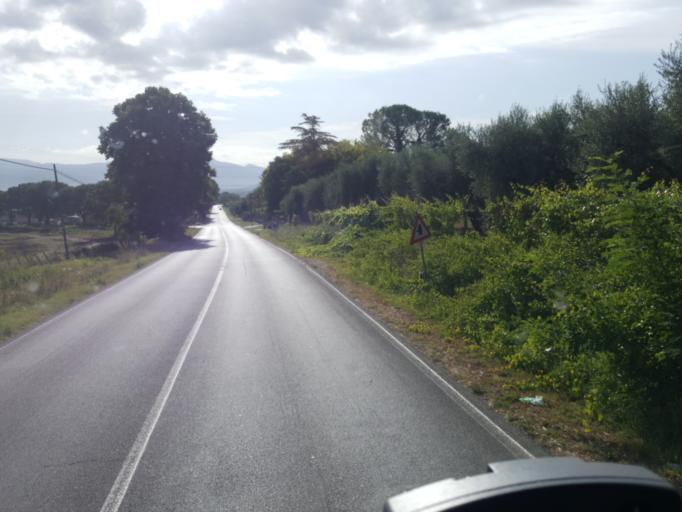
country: IT
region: Latium
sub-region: Citta metropolitana di Roma Capitale
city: Capena
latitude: 42.1297
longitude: 12.5665
